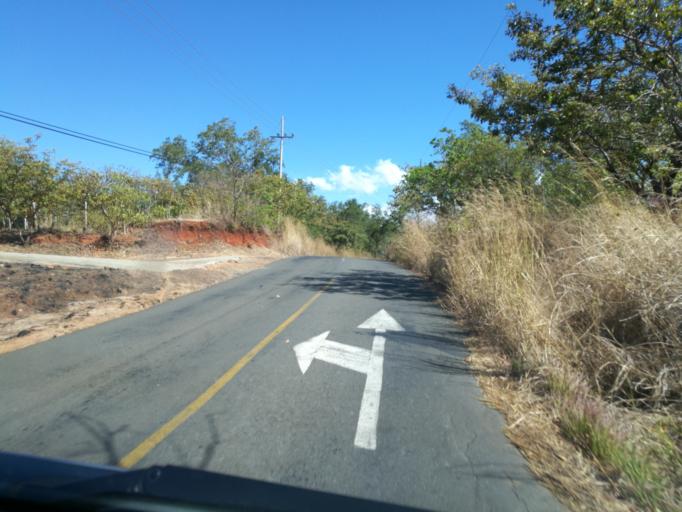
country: CR
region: Guanacaste
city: Liberia
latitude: 10.6696
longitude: -85.4670
